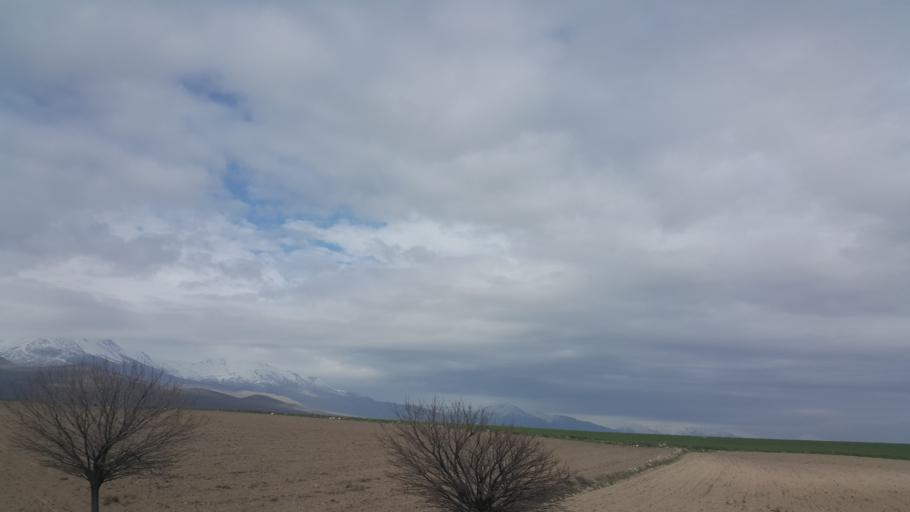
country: TR
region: Aksaray
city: Taspinar
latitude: 38.0107
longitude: 34.0548
